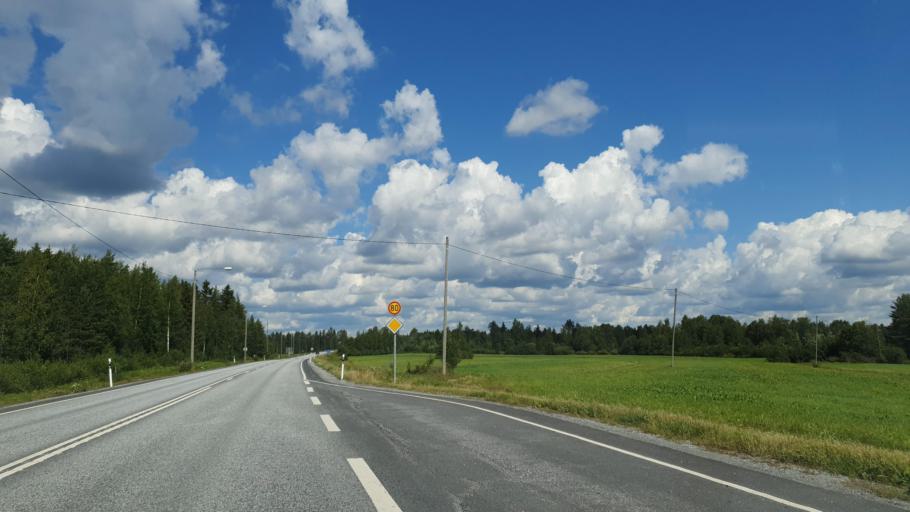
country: FI
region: Northern Savo
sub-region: Ylae-Savo
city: Sonkajaervi
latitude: 63.8697
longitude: 27.4407
